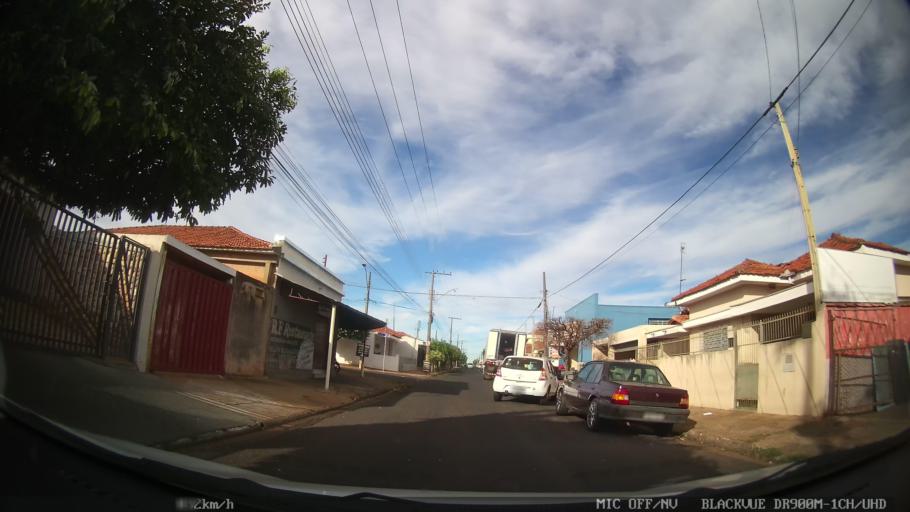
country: BR
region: Sao Paulo
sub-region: Catanduva
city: Catanduva
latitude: -21.1197
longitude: -48.9654
